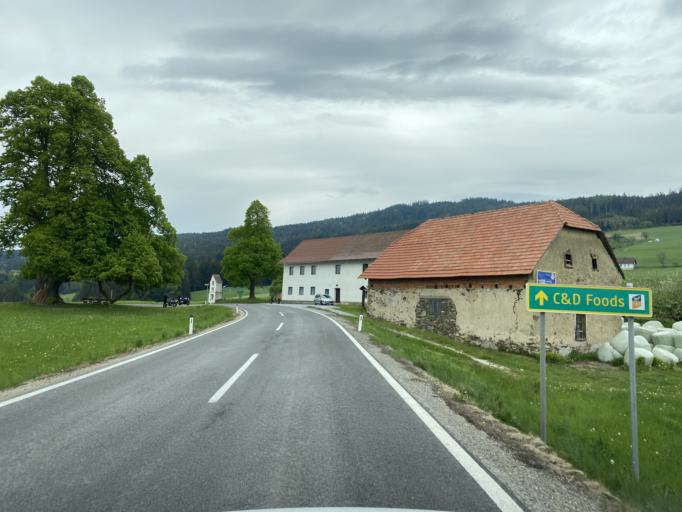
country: AT
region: Styria
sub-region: Politischer Bezirk Weiz
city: Gschaid bei Birkfeld
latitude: 47.3392
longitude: 15.7461
